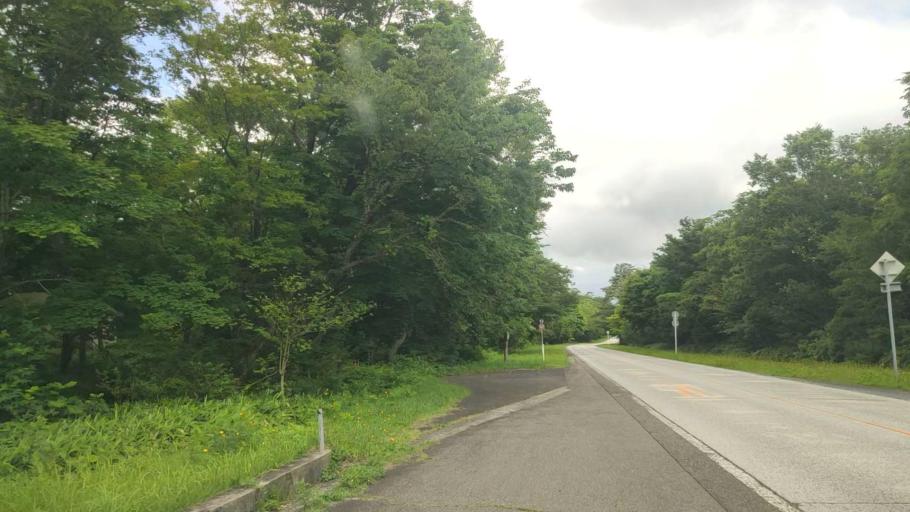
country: JP
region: Tottori
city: Yonago
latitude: 35.3957
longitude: 133.5185
